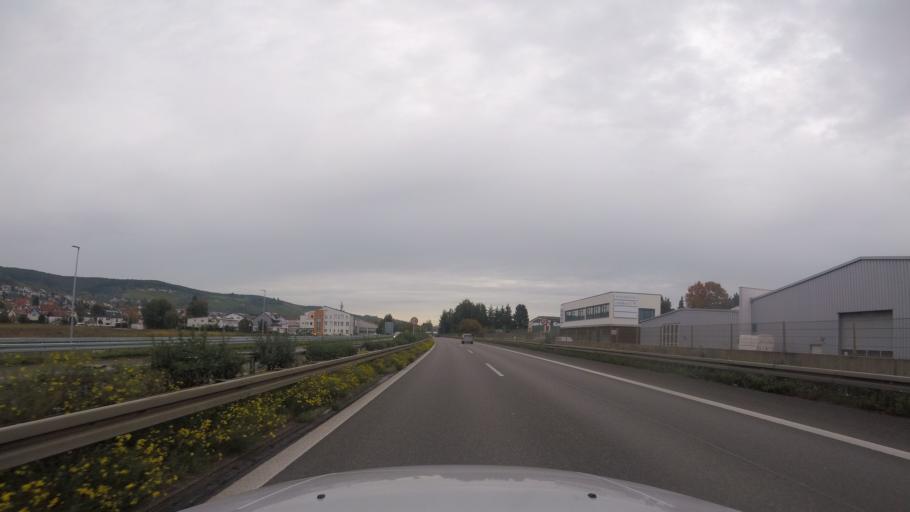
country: DE
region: Baden-Wuerttemberg
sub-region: Regierungsbezirk Stuttgart
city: Weinstadt-Endersbach
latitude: 48.8134
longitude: 9.4135
